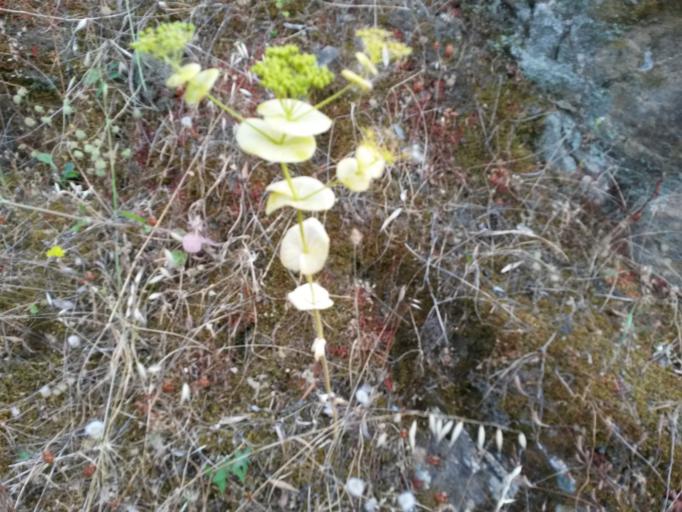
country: GR
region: North Aegean
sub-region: Nomos Lesvou
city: Agiasos
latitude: 39.0986
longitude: 26.3937
